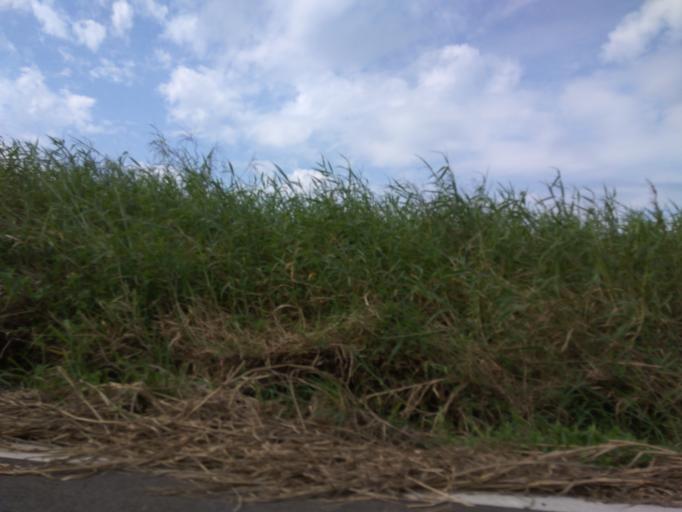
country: TW
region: Taiwan
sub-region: Hsinchu
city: Zhubei
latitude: 24.9600
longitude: 121.0067
